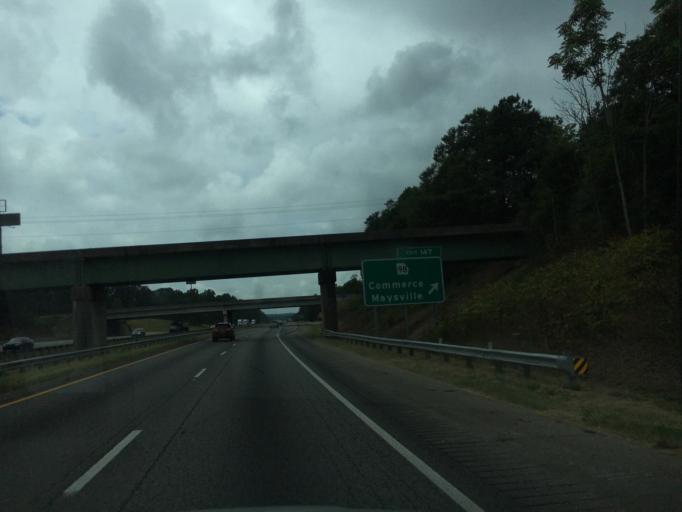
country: US
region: Georgia
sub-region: Jackson County
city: Commerce
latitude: 34.2308
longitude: -83.4978
